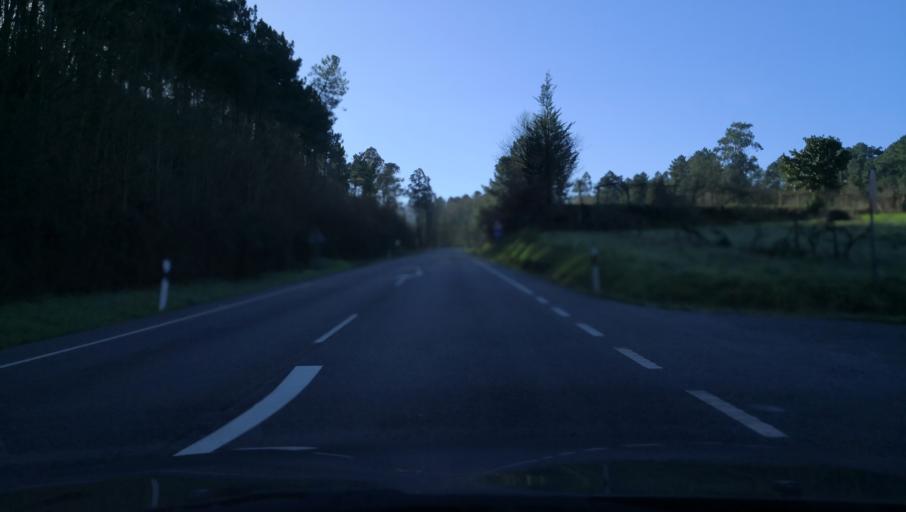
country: ES
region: Galicia
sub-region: Provincia da Coruna
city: Ribeira
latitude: 42.7689
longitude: -8.3981
